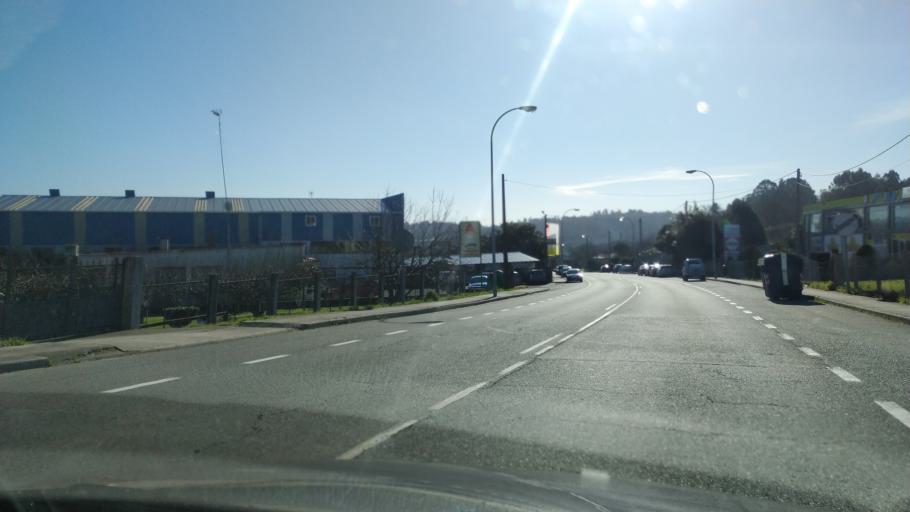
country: ES
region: Galicia
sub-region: Provincia de Pontevedra
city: Silleda
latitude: 42.7398
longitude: -8.3283
